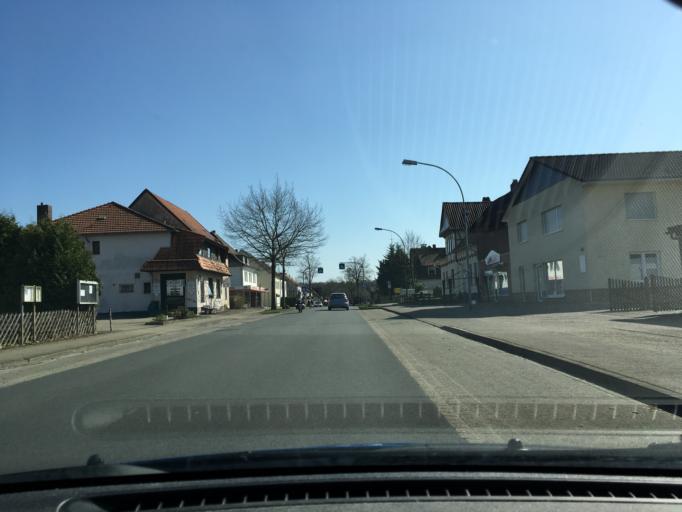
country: DE
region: Lower Saxony
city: Unterluss
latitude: 52.8399
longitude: 10.2962
